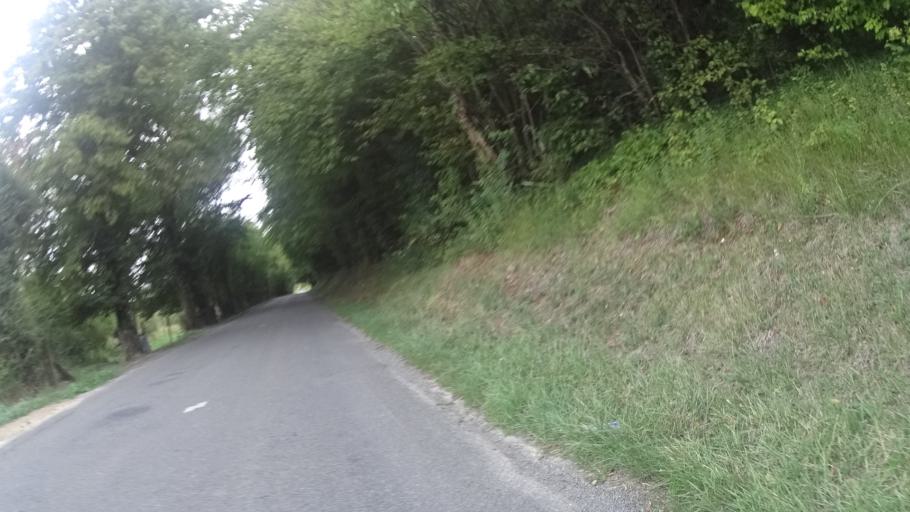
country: FR
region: Picardie
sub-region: Departement de l'Aisne
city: Guise
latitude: 49.9094
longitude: 3.5676
